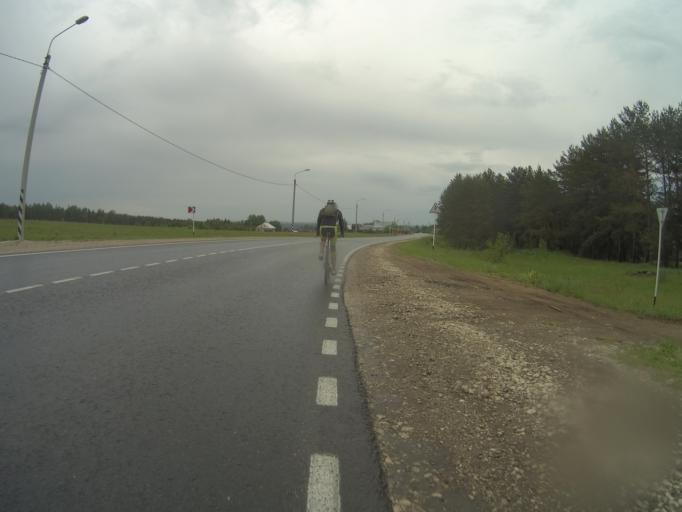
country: RU
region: Vladimir
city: Raduzhnyy
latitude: 56.0108
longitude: 40.3068
